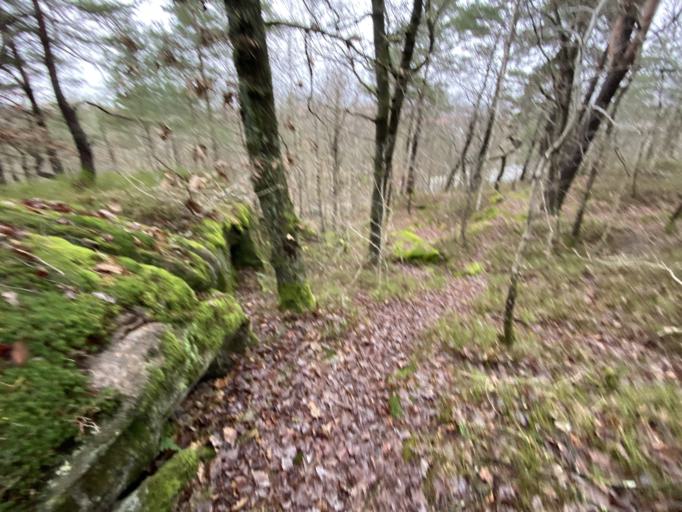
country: SE
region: Vaestra Goetaland
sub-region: Goteborg
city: Eriksbo
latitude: 57.7153
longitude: 12.0420
